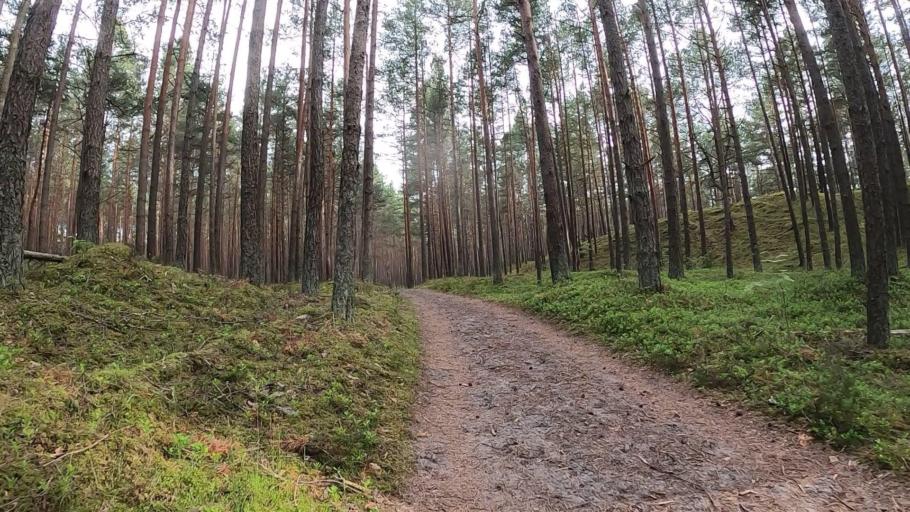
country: LV
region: Riga
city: Jaunciems
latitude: 57.0959
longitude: 24.1639
